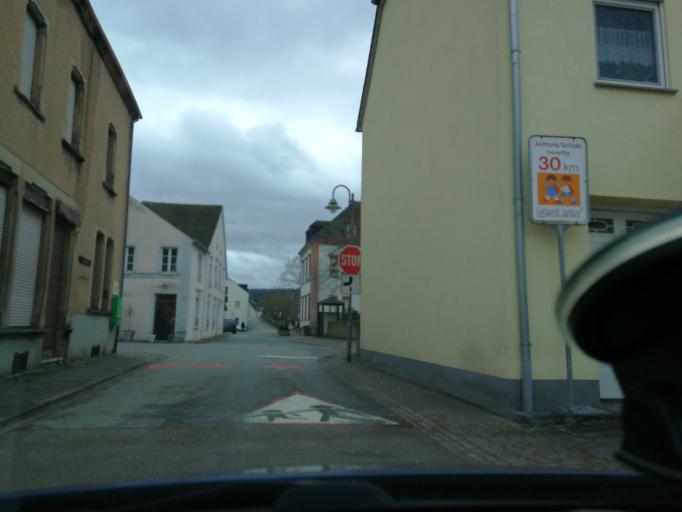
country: DE
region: Rheinland-Pfalz
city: Oberbillig
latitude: 49.7244
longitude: 6.4972
